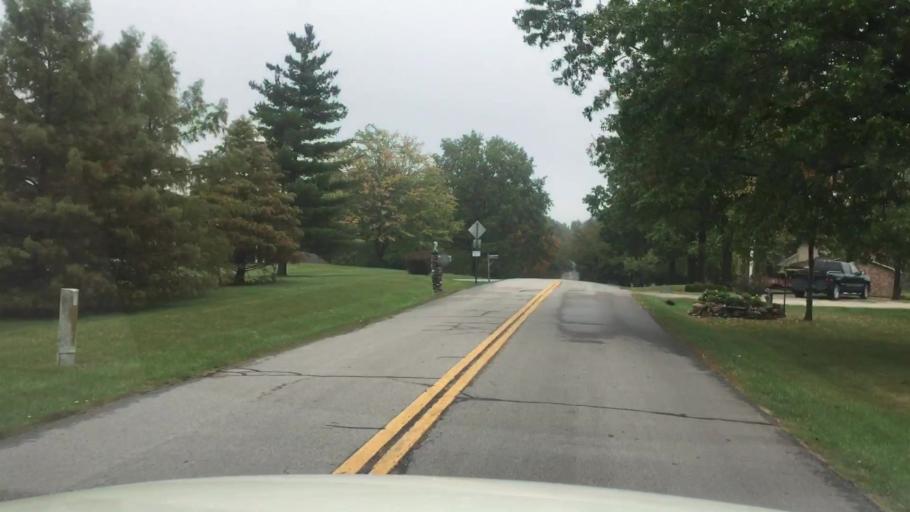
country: US
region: Missouri
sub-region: Boone County
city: Columbia
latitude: 38.8573
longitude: -92.3151
